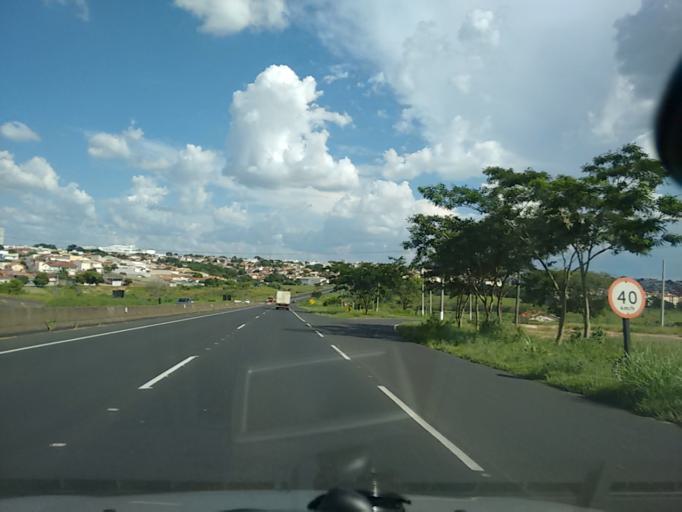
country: BR
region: Sao Paulo
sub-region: Marilia
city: Marilia
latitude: -22.1878
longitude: -49.9689
